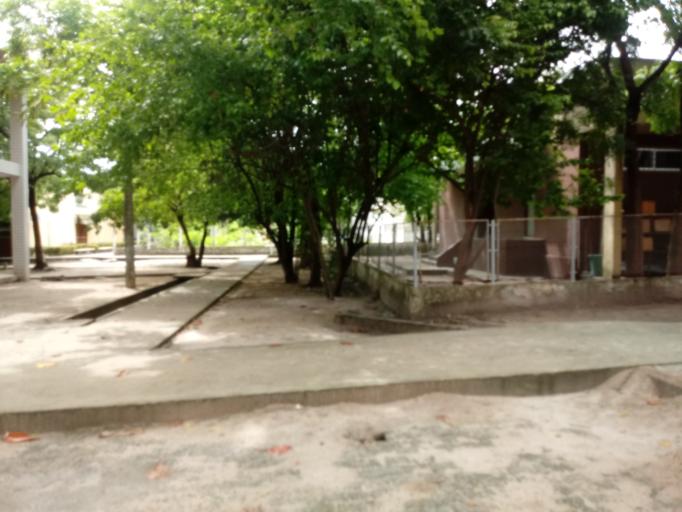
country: BR
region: Ceara
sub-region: Fortaleza
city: Fortaleza
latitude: -3.7452
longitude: -38.5749
